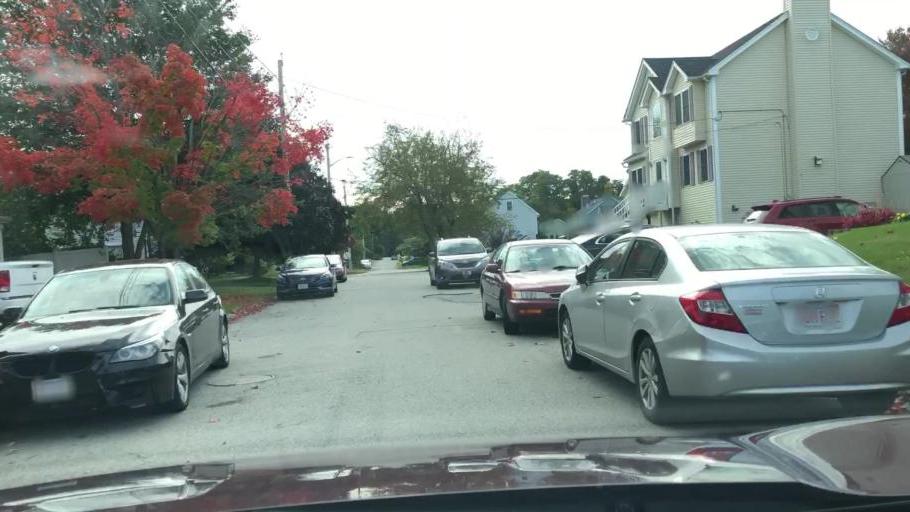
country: US
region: Massachusetts
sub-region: Essex County
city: North Andover
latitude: 42.7324
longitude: -71.1279
